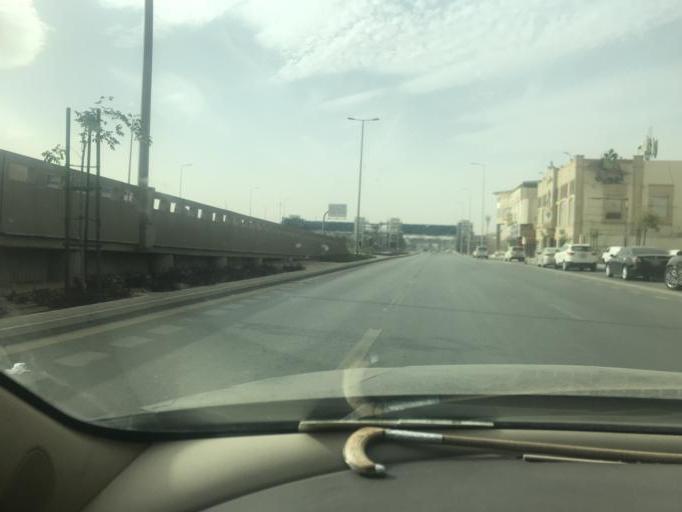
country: SA
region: Ar Riyad
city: Riyadh
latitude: 24.7774
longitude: 46.6649
